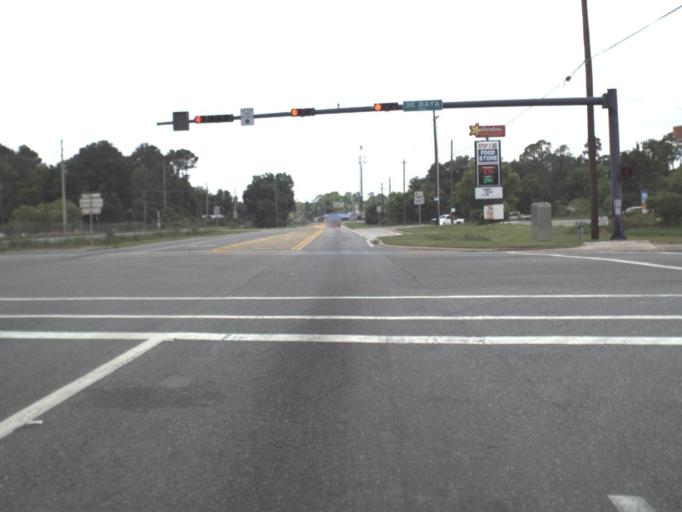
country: US
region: Florida
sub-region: Columbia County
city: Watertown
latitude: 30.1838
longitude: -82.6000
